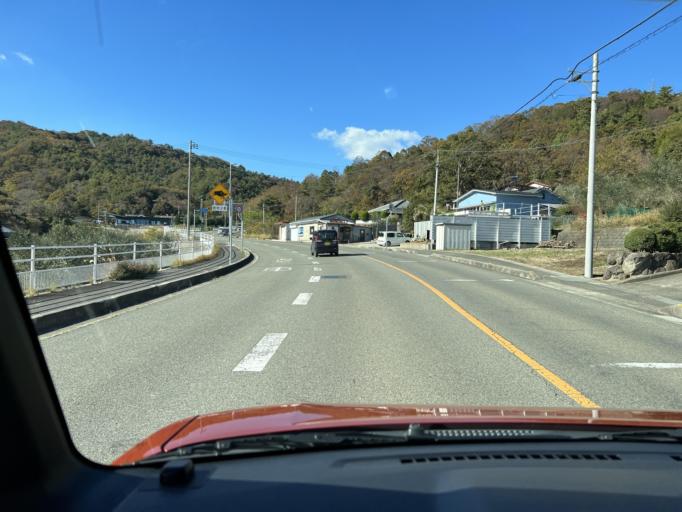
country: JP
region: Kagawa
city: Tonosho
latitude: 34.4711
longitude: 134.2621
